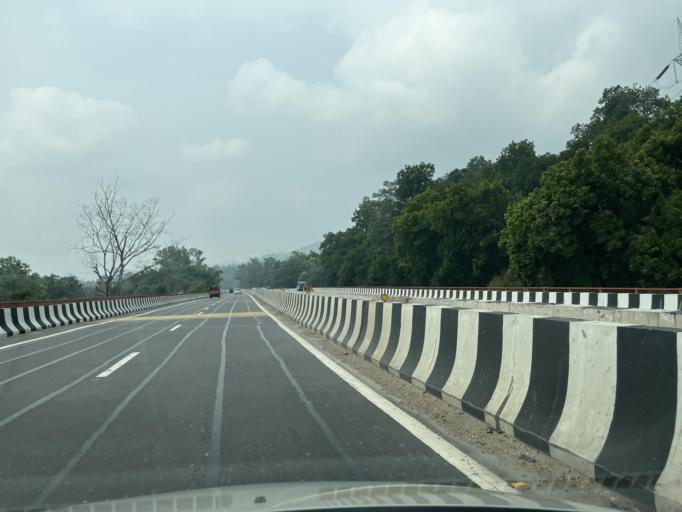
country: IN
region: Uttarakhand
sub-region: Dehradun
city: Raiwala
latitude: 30.0126
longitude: 78.1943
